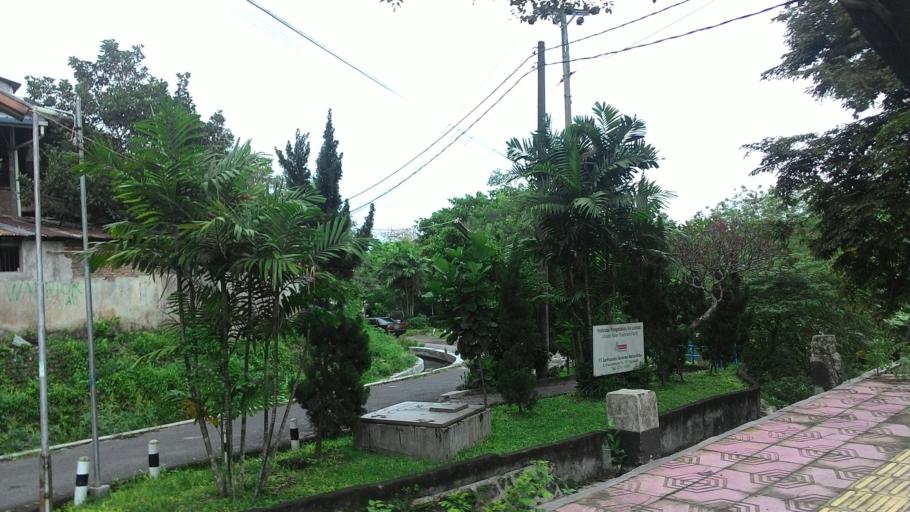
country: ID
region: Daerah Istimewa Yogyakarta
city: Yogyakarta
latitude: -7.8021
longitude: 110.3971
